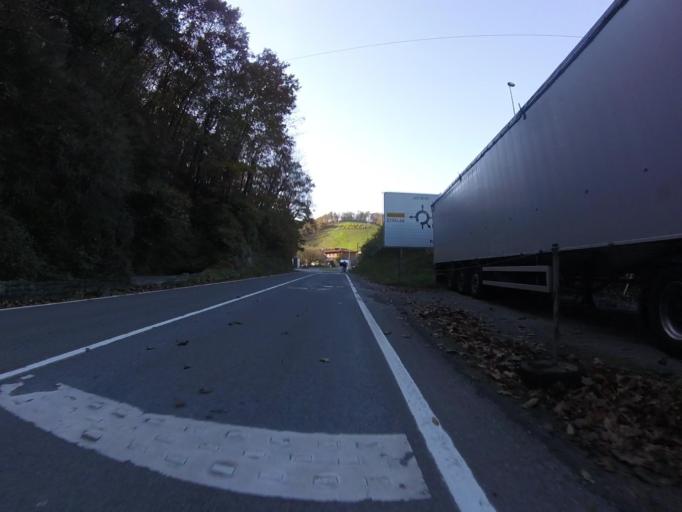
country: ES
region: Navarre
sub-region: Provincia de Navarra
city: Lesaka
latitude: 43.2439
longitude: -1.6695
